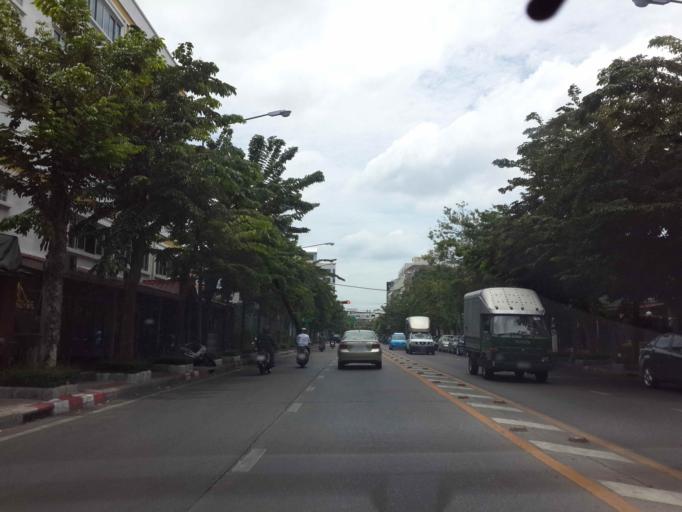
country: TH
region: Bangkok
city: Samphanthawong
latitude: 13.7276
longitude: 100.5186
